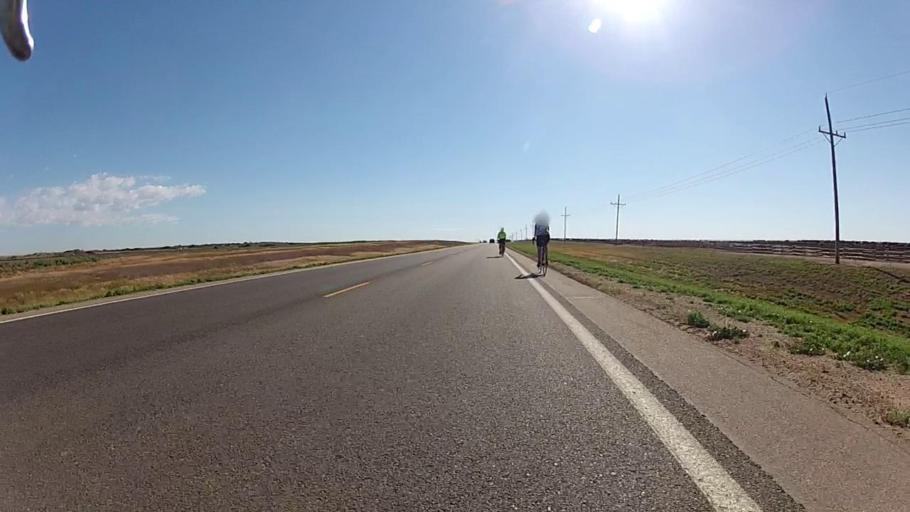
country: US
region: Kansas
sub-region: Gray County
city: Cimarron
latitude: 37.5742
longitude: -100.5292
